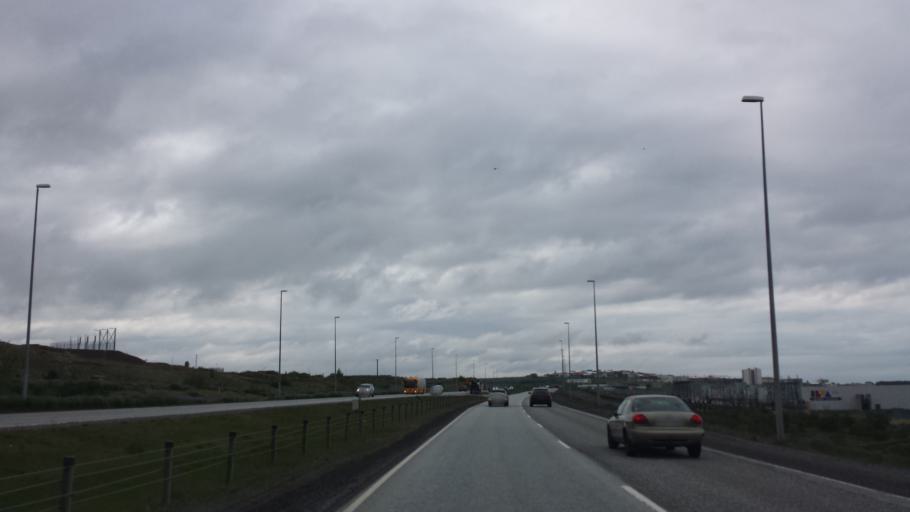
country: IS
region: Capital Region
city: Mosfellsbaer
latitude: 64.1489
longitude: -21.7448
